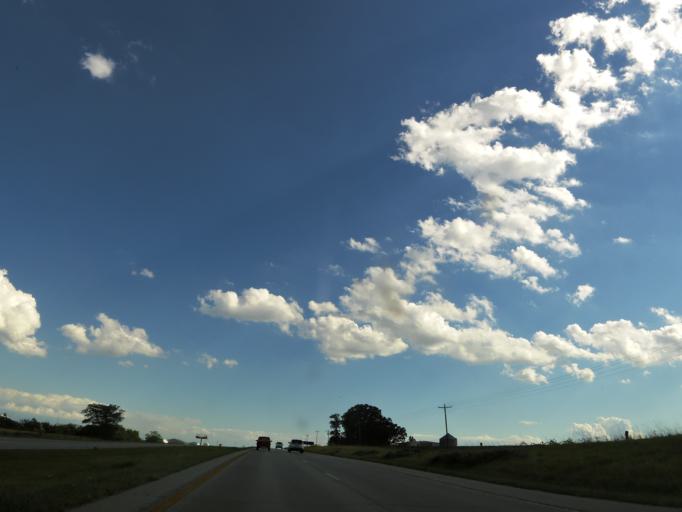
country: US
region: Missouri
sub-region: Marion County
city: Palmyra
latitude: 39.8853
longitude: -91.5250
